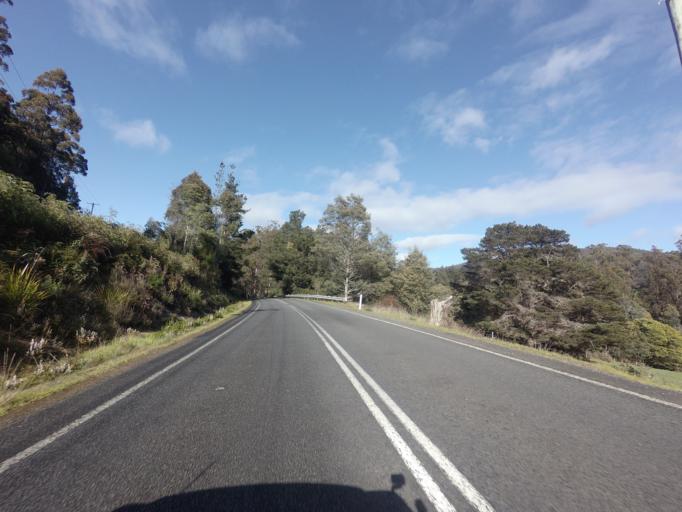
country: AU
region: Tasmania
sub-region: Huon Valley
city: Cygnet
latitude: -43.2749
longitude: 147.0094
